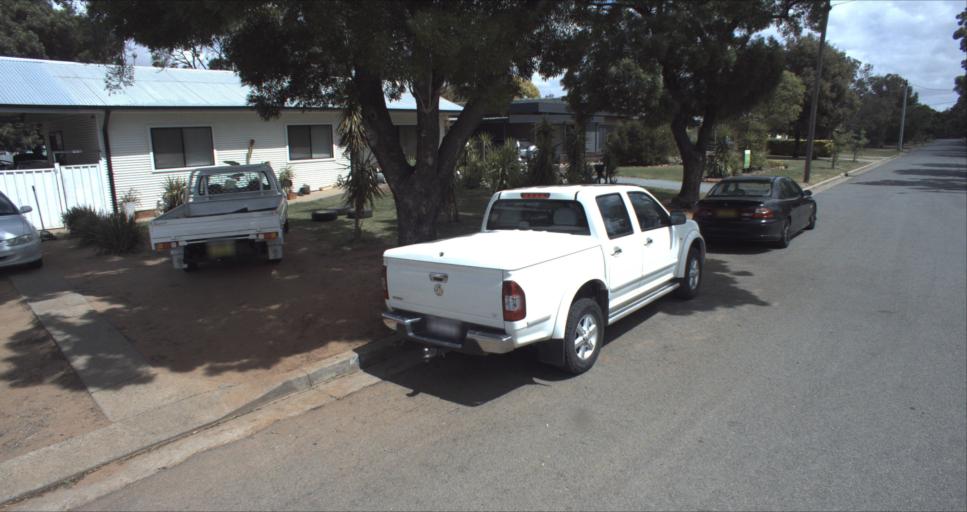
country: AU
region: New South Wales
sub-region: Leeton
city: Leeton
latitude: -34.5546
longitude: 146.3908
